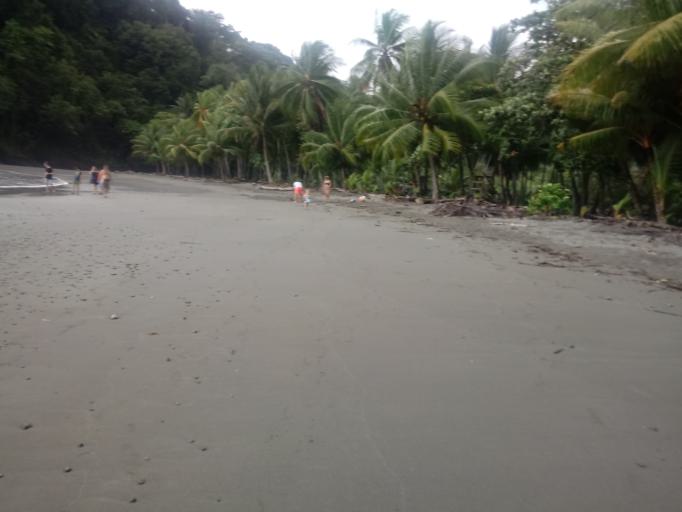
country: CR
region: San Jose
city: Mercedes
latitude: 9.0909
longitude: -83.6771
